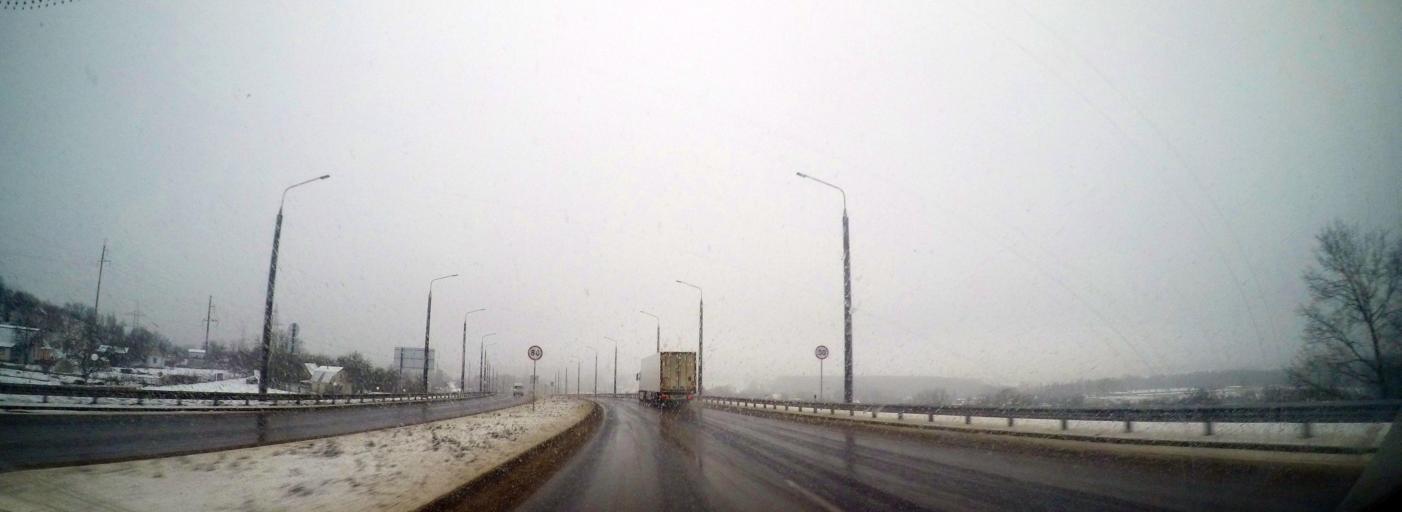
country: BY
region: Grodnenskaya
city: Hrodna
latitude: 53.6628
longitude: 23.8863
